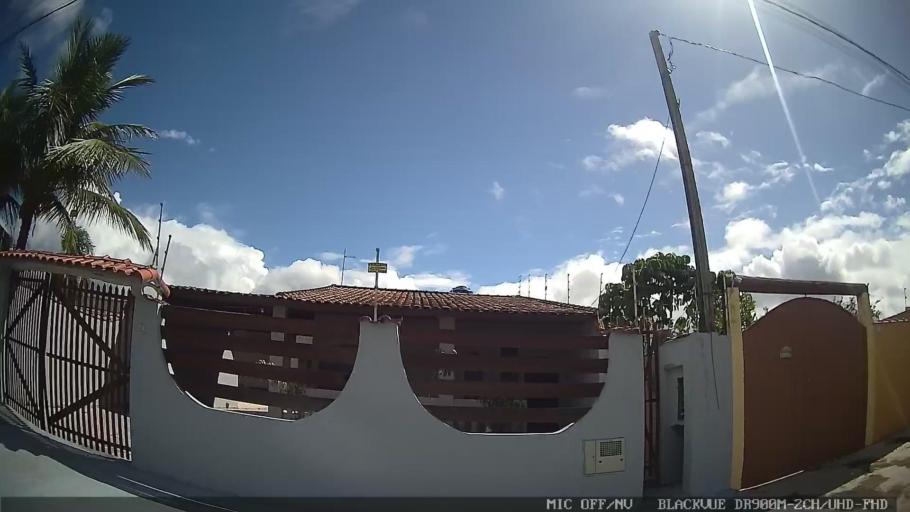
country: BR
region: Sao Paulo
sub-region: Itanhaem
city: Itanhaem
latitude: -24.2250
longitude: -46.8616
